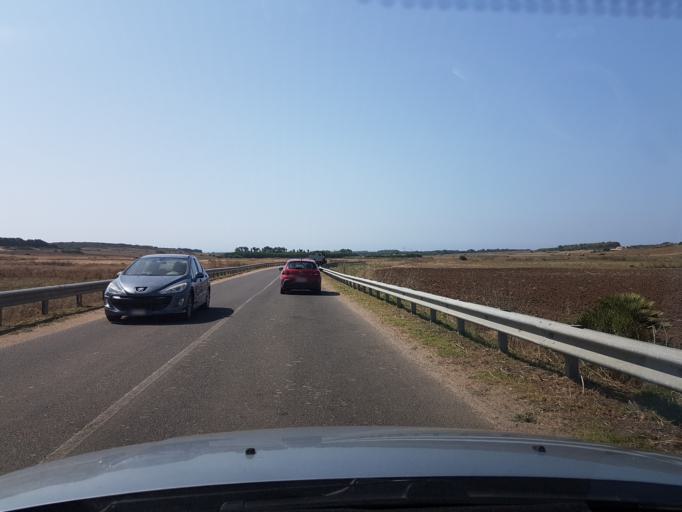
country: IT
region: Sardinia
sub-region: Provincia di Oristano
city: Cabras
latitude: 39.9370
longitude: 8.4432
